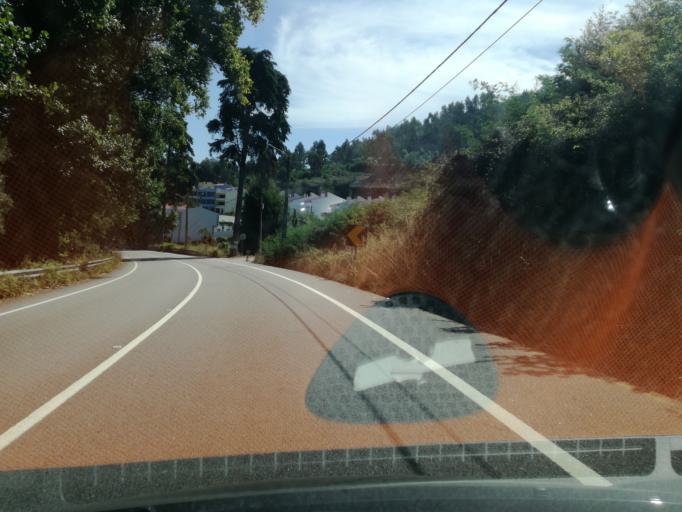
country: ES
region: Galicia
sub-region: Provincia de Pontevedra
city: O Rosal
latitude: 41.9005
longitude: -8.8094
